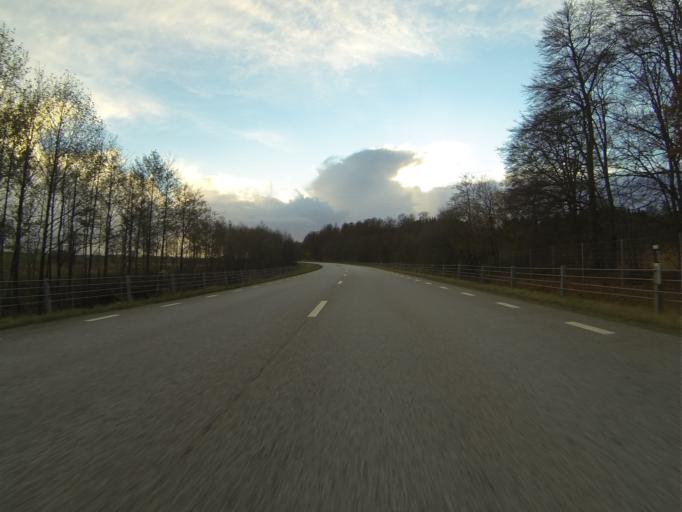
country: SE
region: Skane
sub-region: Lunds Kommun
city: Genarp
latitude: 55.5242
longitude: 13.3373
